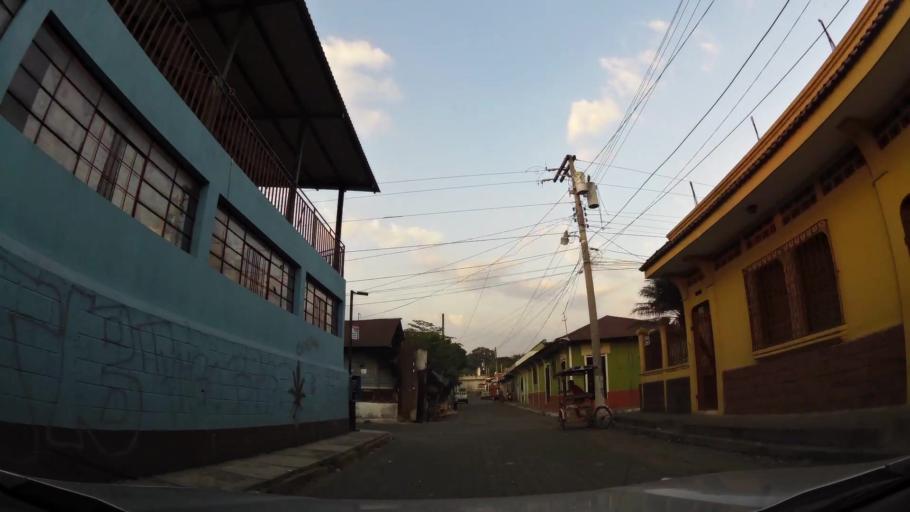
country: GT
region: Retalhuleu
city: San Sebastian
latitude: 14.5634
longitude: -91.6471
